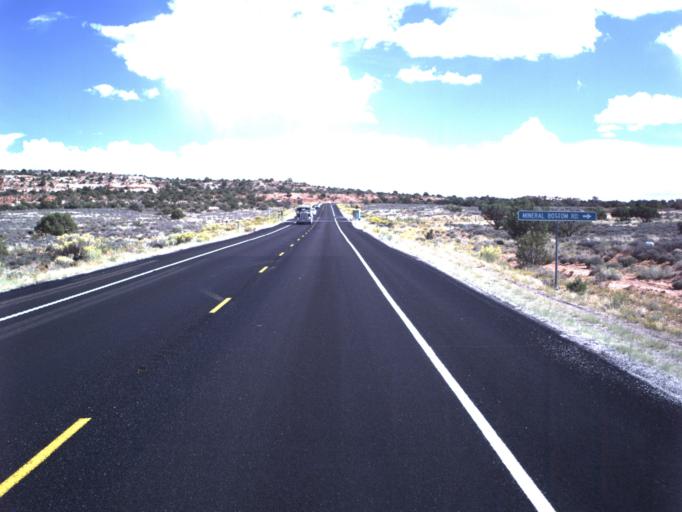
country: US
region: Utah
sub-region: Grand County
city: Moab
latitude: 38.5846
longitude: -109.8030
